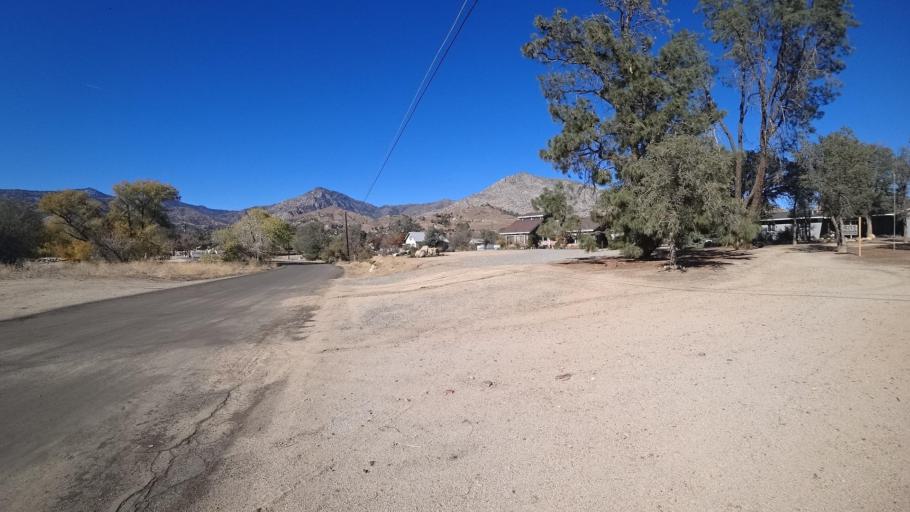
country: US
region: California
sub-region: Kern County
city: Wofford Heights
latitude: 35.7055
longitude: -118.4471
